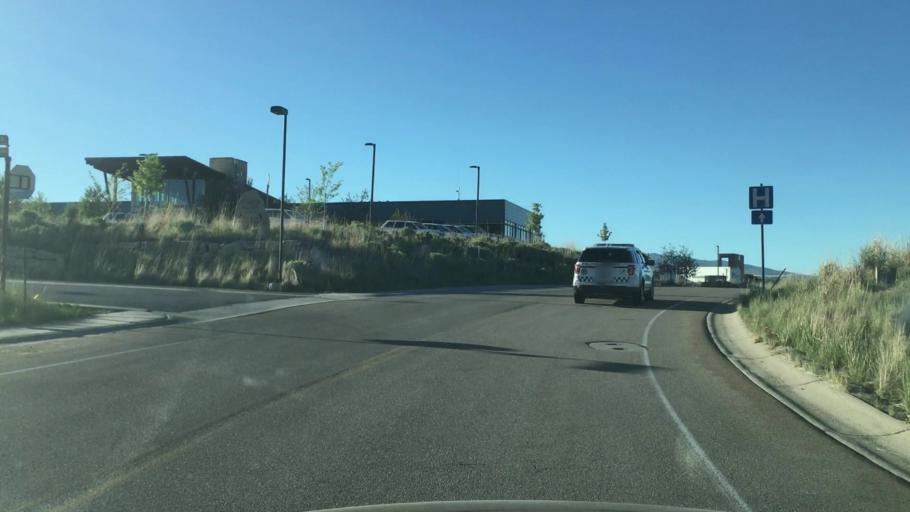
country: US
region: Utah
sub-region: Summit County
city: Park City
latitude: 40.6831
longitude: -111.4664
